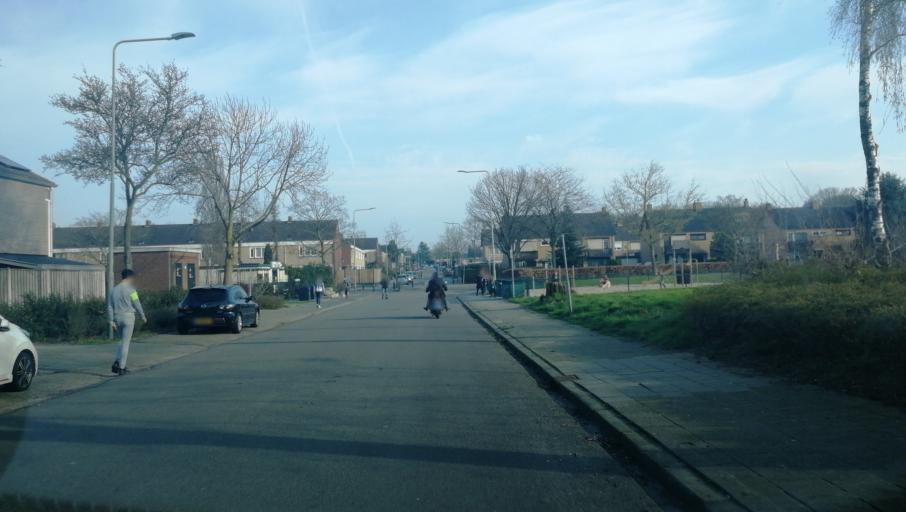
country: NL
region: Limburg
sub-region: Gemeente Venlo
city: Tegelen
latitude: 51.3348
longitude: 6.1550
